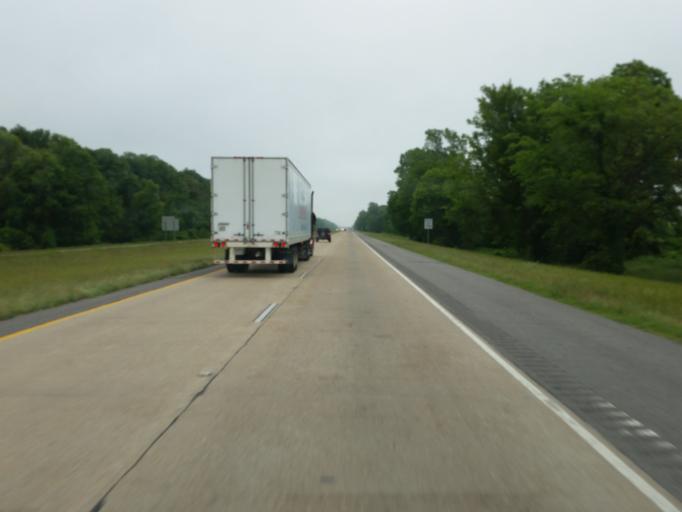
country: US
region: Louisiana
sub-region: Madison Parish
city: Tallulah
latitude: 32.3768
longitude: -91.1607
